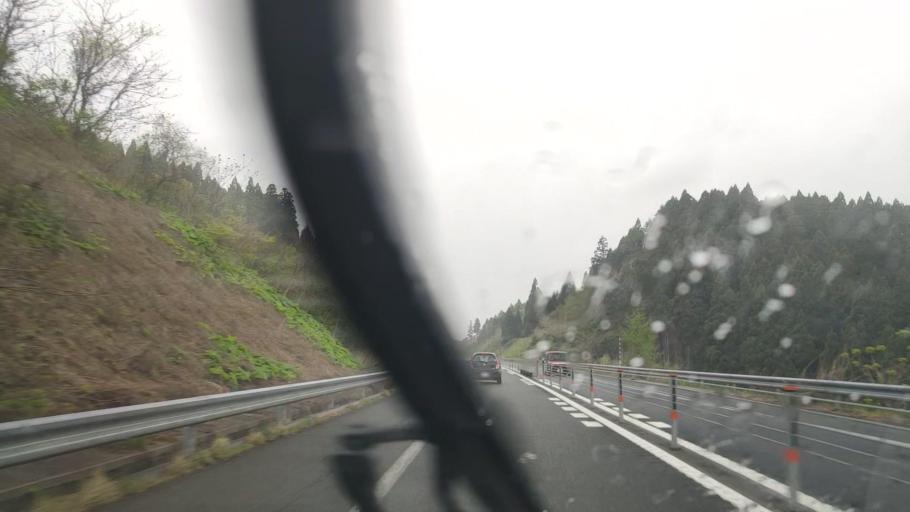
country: JP
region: Akita
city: Noshiromachi
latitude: 40.1984
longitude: 140.1279
